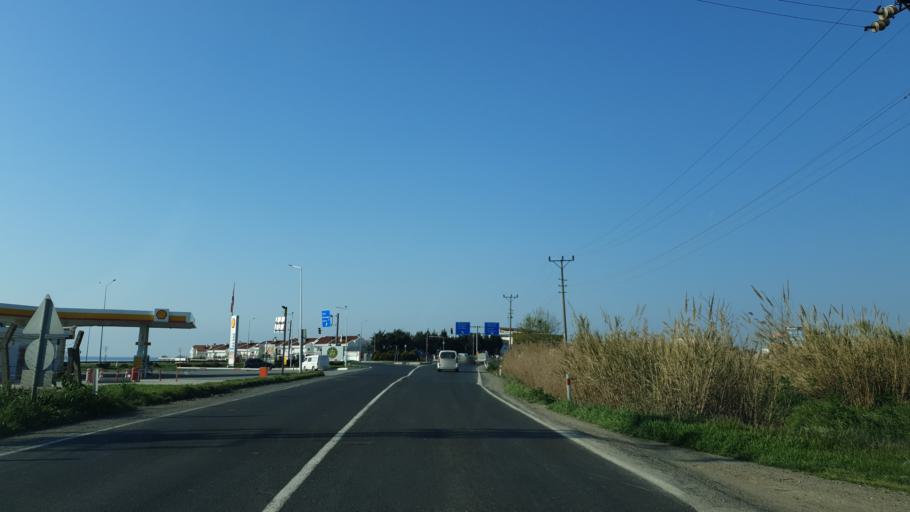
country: TR
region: Tekirdag
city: Corlu
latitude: 41.0114
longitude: 27.7175
